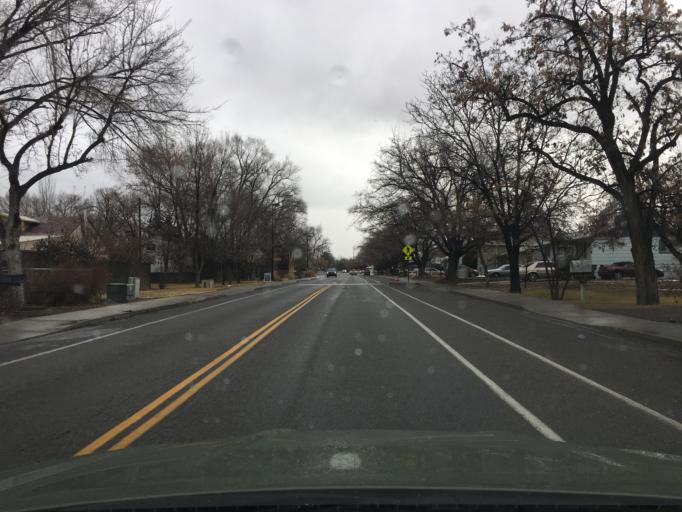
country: US
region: Colorado
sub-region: Mesa County
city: Grand Junction
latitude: 39.0810
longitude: -108.5746
